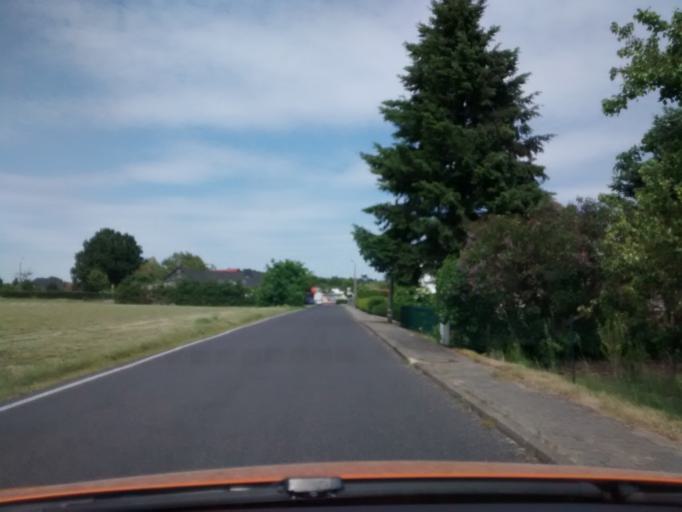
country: DE
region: Brandenburg
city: Ihlow
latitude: 51.9238
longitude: 13.3322
